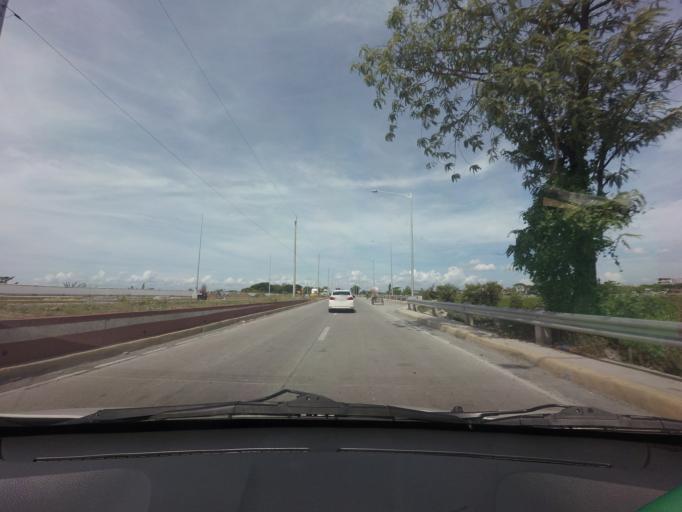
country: PH
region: Calabarzon
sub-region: Province of Rizal
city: Taguig
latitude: 14.5298
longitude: 121.0941
